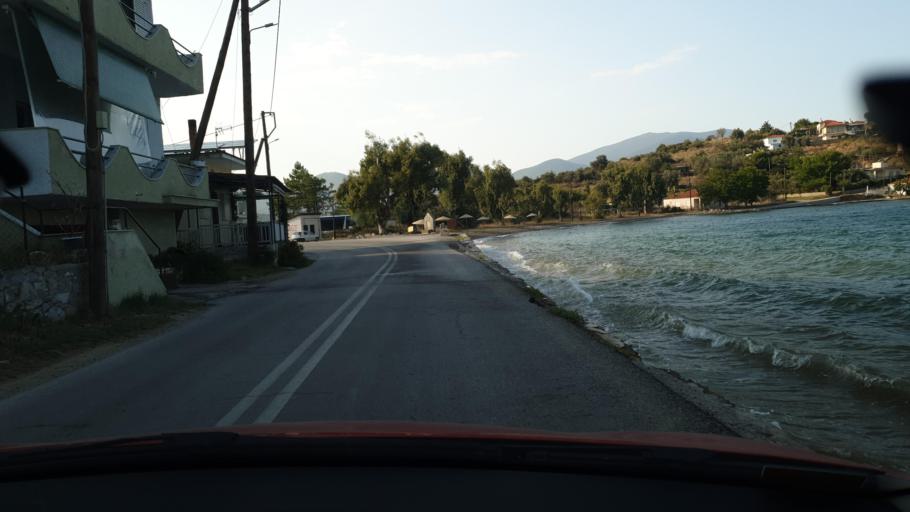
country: GR
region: Thessaly
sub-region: Nomos Magnisias
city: Pteleos
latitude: 39.0089
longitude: 22.9581
